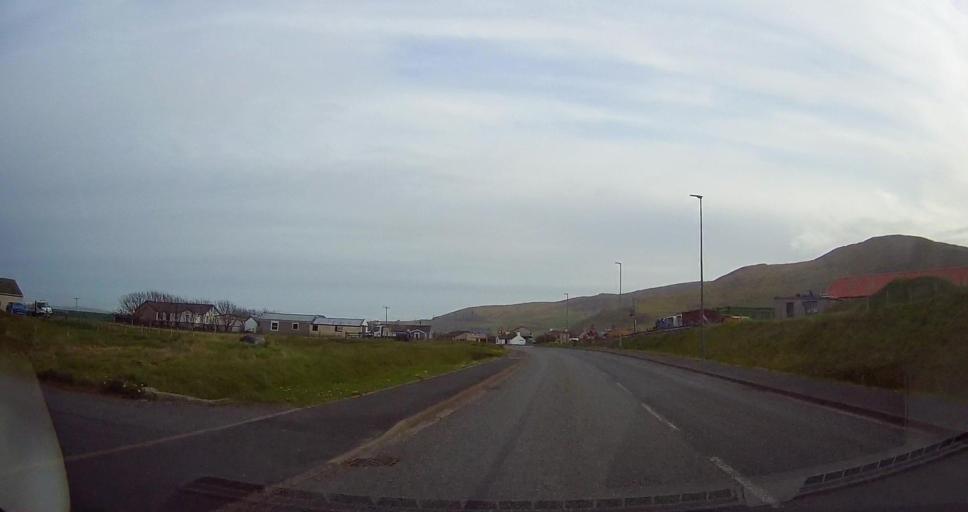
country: GB
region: Scotland
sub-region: Shetland Islands
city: Sandwick
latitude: 60.0419
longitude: -1.2295
